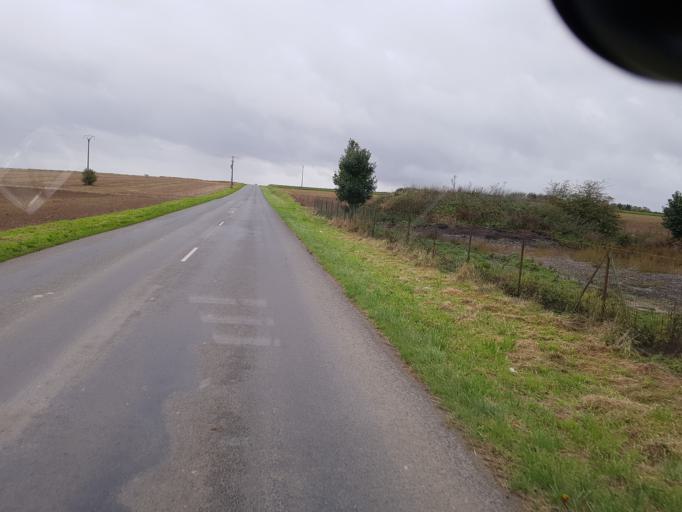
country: FR
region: Nord-Pas-de-Calais
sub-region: Departement du Pas-de-Calais
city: Neuville-Saint-Vaast
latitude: 50.3470
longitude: 2.7448
